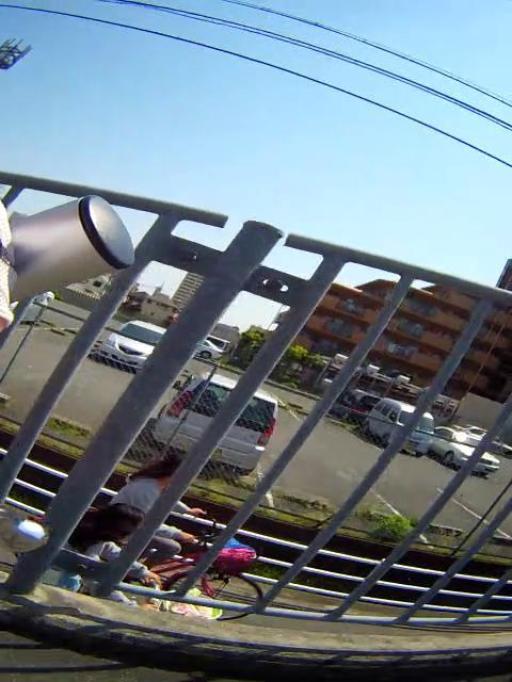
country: JP
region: Osaka
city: Matsubara
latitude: 34.5760
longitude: 135.5510
